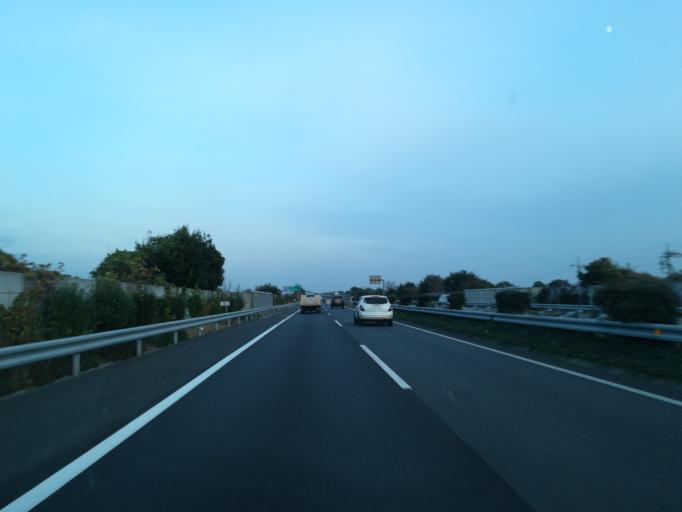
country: JP
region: Gunma
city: Isesaki
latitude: 36.3511
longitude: 139.1542
